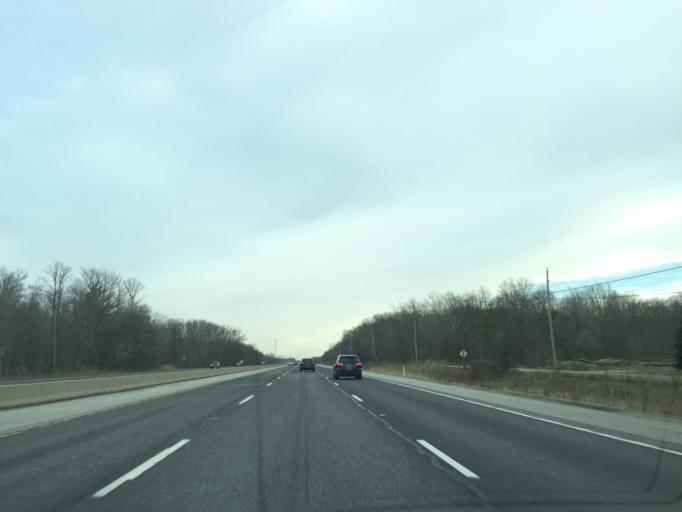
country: US
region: Indiana
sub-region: LaPorte County
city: Long Beach
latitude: 41.7313
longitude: -86.7963
